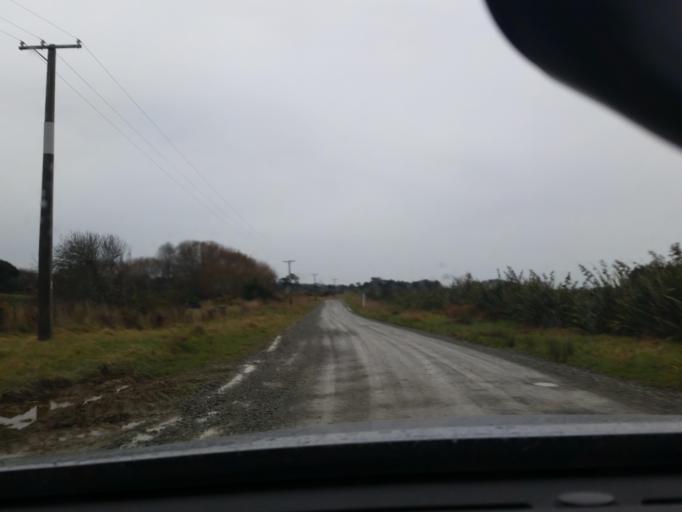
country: NZ
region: Southland
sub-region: Southland District
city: Winton
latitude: -46.2434
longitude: 168.4742
